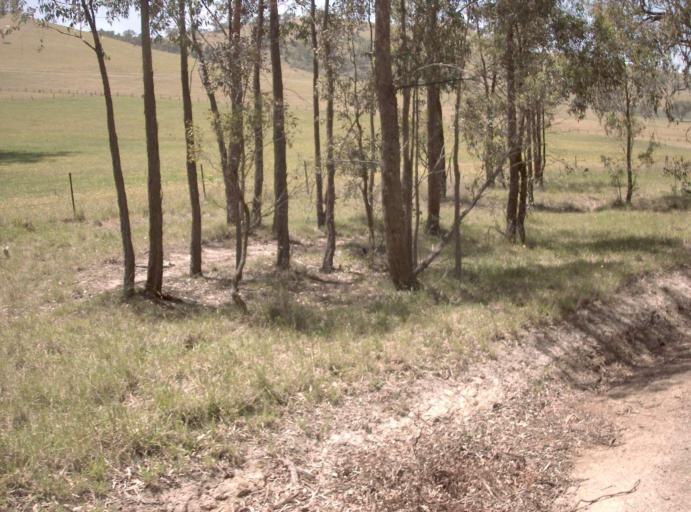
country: AU
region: Victoria
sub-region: East Gippsland
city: Bairnsdale
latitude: -37.3416
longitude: 147.7933
